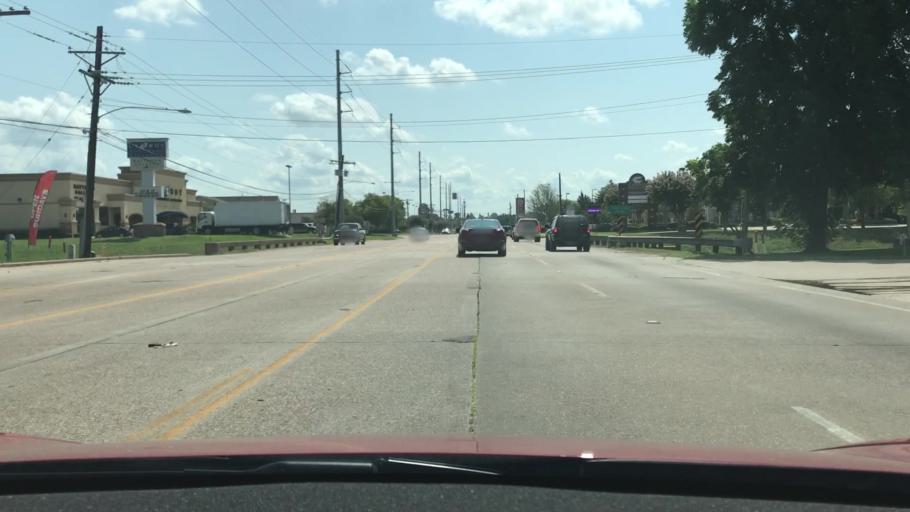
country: US
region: Louisiana
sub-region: Bossier Parish
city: Bossier City
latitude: 32.4434
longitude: -93.7251
